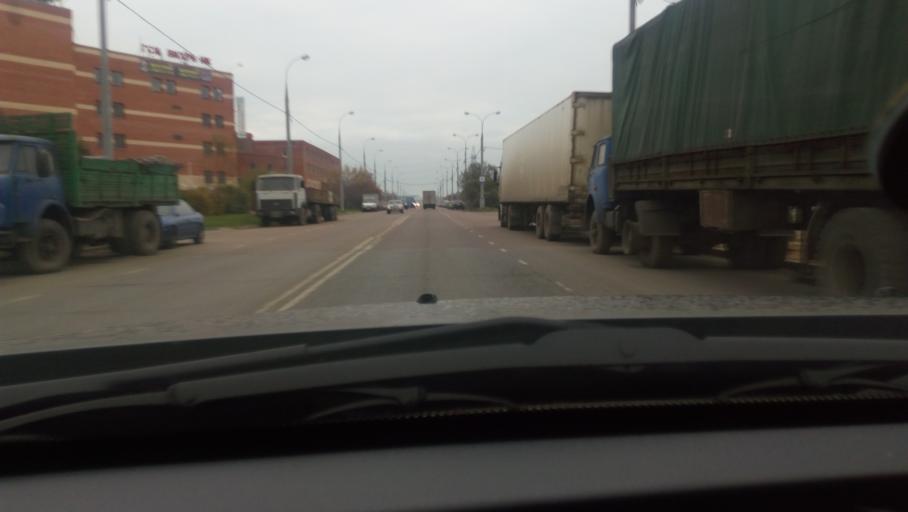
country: RU
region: Moskovskaya
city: Reutov
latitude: 55.7444
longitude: 37.8817
